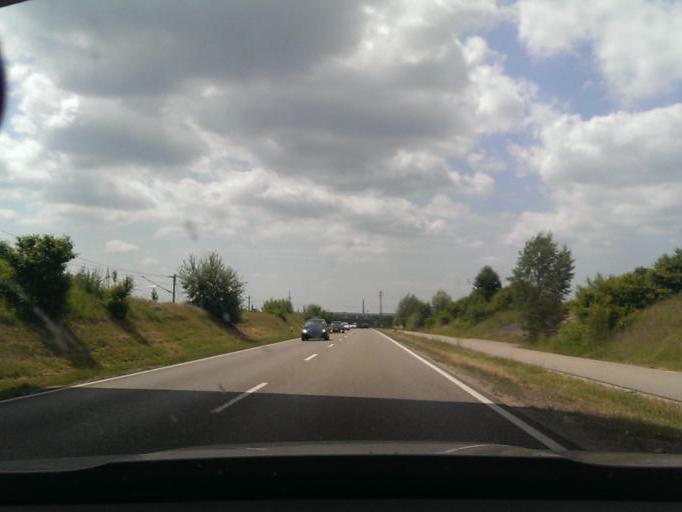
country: DE
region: Bavaria
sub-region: Upper Bavaria
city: Wettstetten
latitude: 48.8054
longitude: 11.4269
